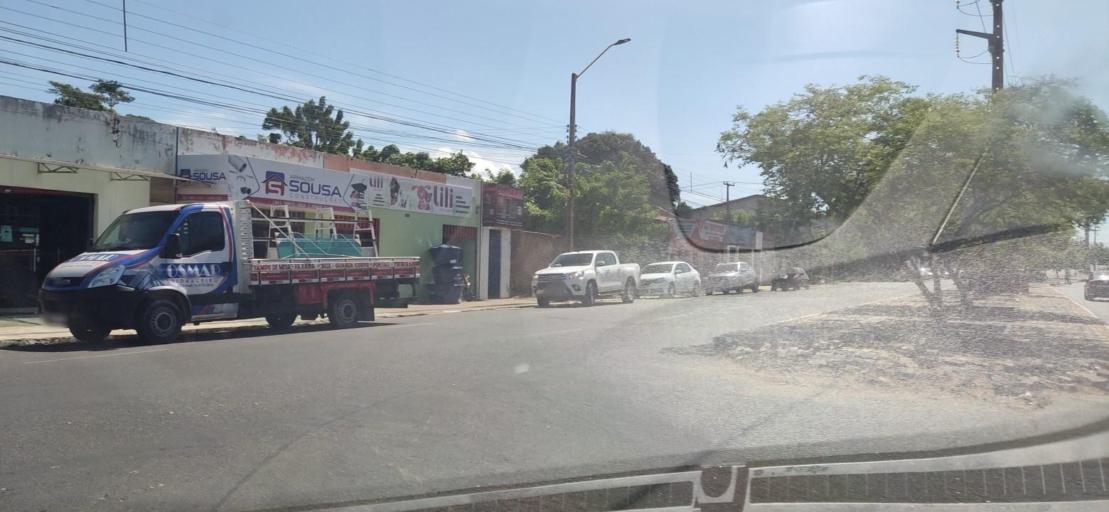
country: BR
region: Piaui
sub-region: Teresina
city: Teresina
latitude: -5.1181
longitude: -42.8005
